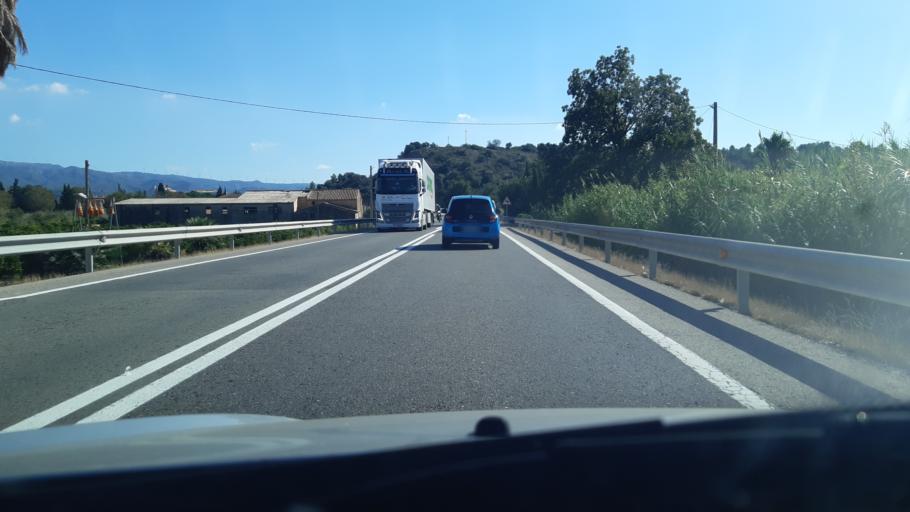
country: ES
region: Catalonia
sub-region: Provincia de Tarragona
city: Tivenys
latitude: 40.8843
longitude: 0.4932
